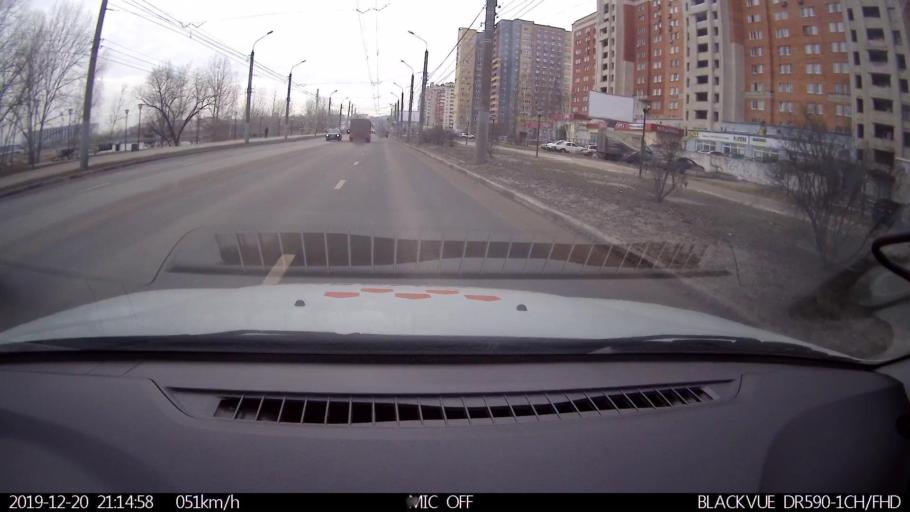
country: RU
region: Nizjnij Novgorod
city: Nizhniy Novgorod
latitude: 56.3370
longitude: 43.9388
